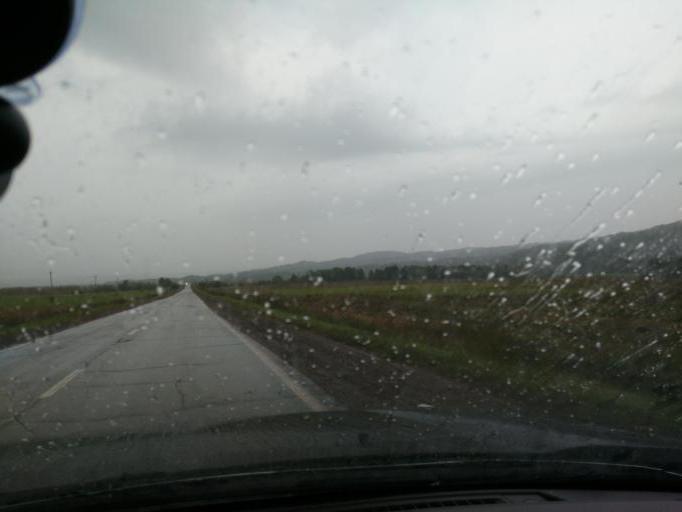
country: RU
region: Perm
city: Barda
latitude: 56.9307
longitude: 55.6716
